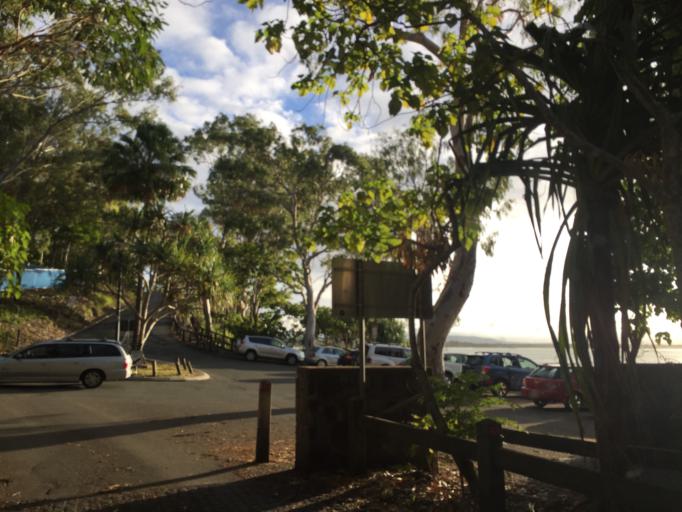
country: AU
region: Queensland
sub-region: Sunshine Coast
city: Noosa Heads
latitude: -26.3818
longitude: 153.0985
